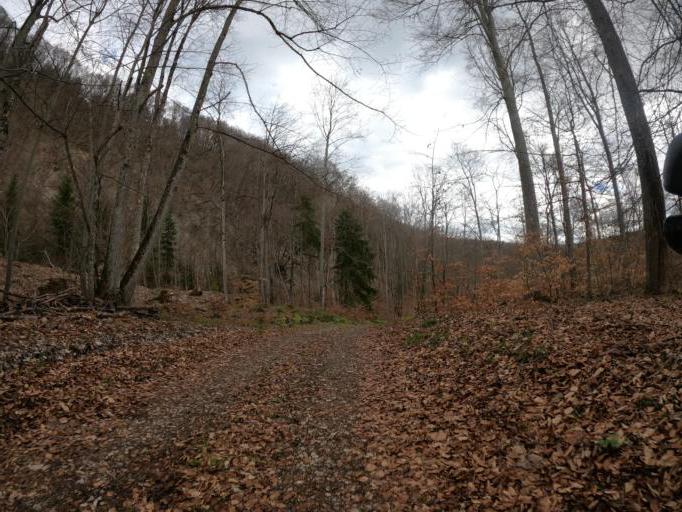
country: DE
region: Baden-Wuerttemberg
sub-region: Tuebingen Region
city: Jungingen
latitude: 48.3674
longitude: 9.0504
